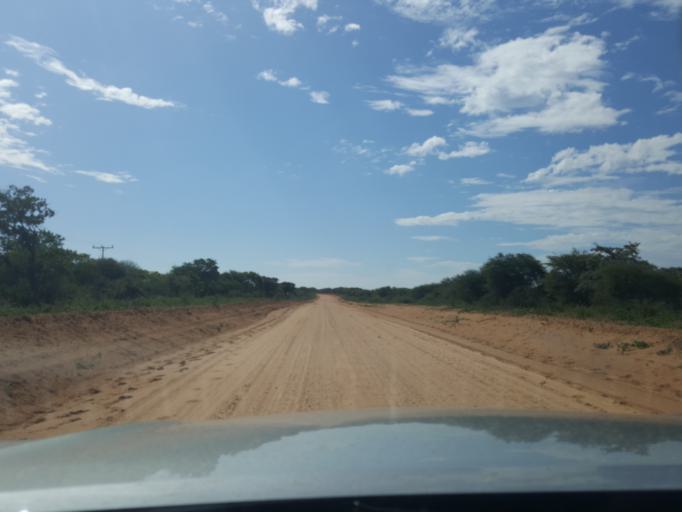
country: BW
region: Kweneng
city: Khudumelapye
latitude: -23.8112
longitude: 24.8198
